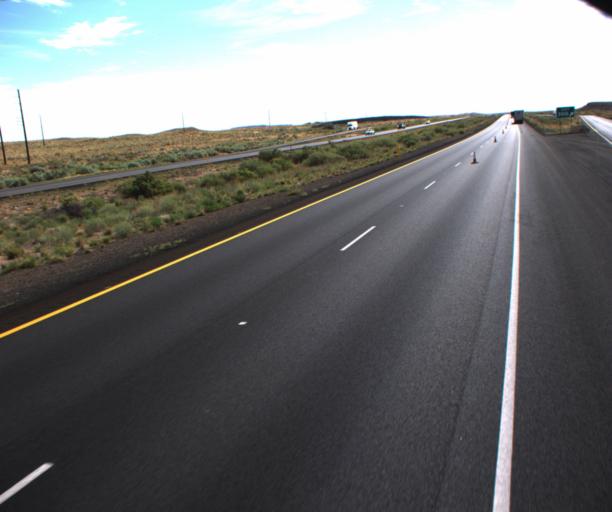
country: US
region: Arizona
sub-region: Navajo County
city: Holbrook
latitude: 34.9908
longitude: -109.9654
